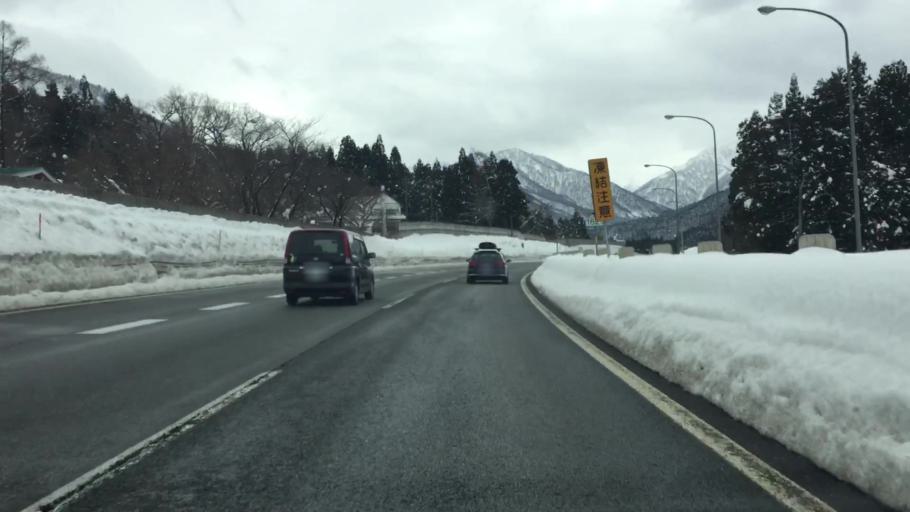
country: JP
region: Niigata
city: Shiozawa
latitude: 36.9038
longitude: 138.8475
